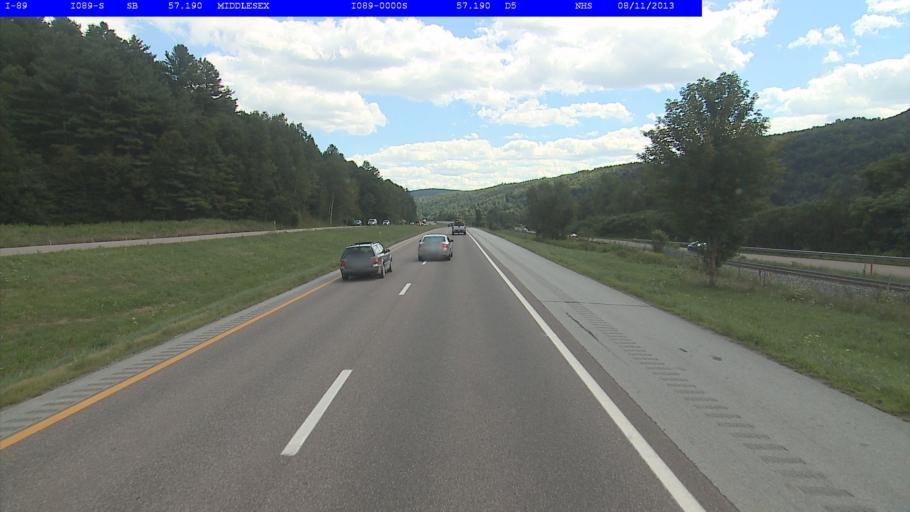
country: US
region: Vermont
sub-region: Washington County
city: Montpelier
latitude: 44.2847
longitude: -72.6621
